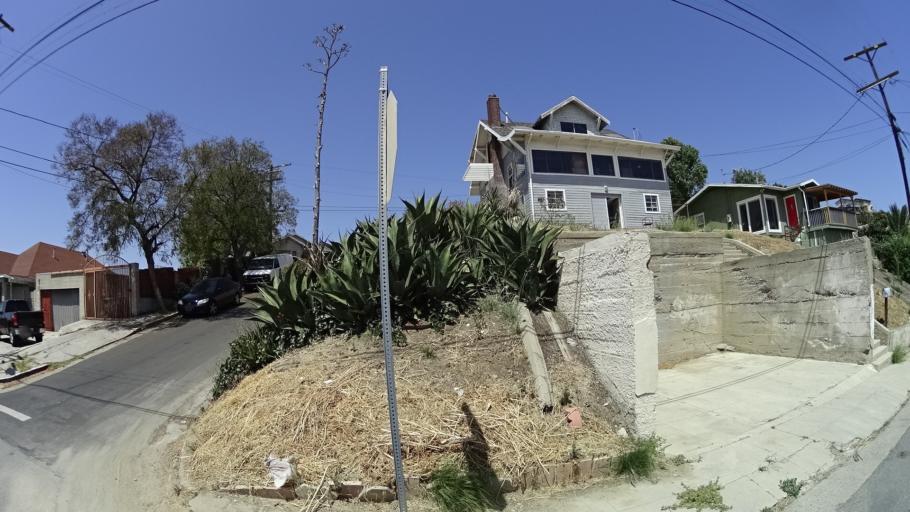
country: US
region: California
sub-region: Los Angeles County
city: Los Angeles
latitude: 34.0776
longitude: -118.2087
